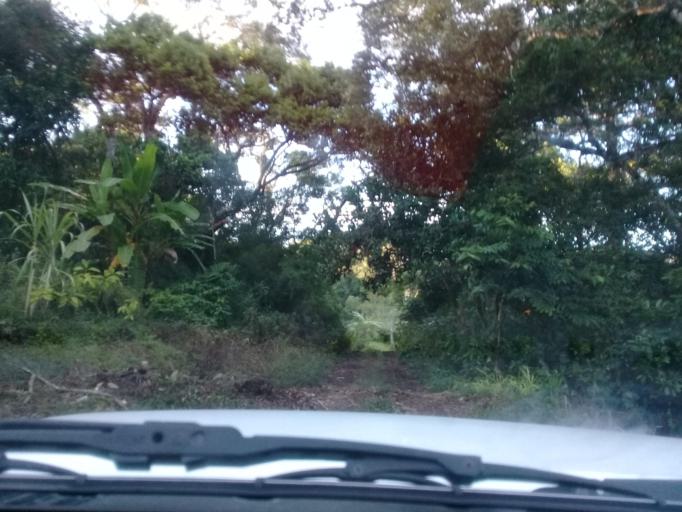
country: MX
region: Veracruz
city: Catemaco
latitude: 18.4309
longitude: -95.0886
